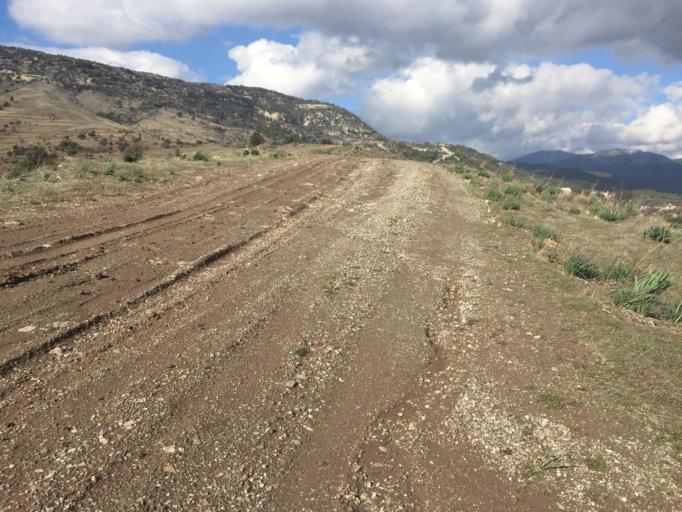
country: CY
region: Limassol
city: Pachna
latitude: 34.8810
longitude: 32.6553
